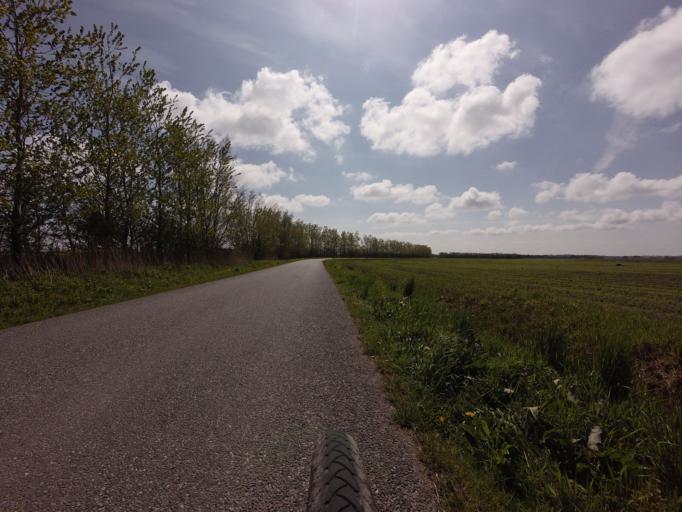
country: DK
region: North Denmark
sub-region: Jammerbugt Kommune
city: Brovst
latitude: 57.1391
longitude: 9.5235
